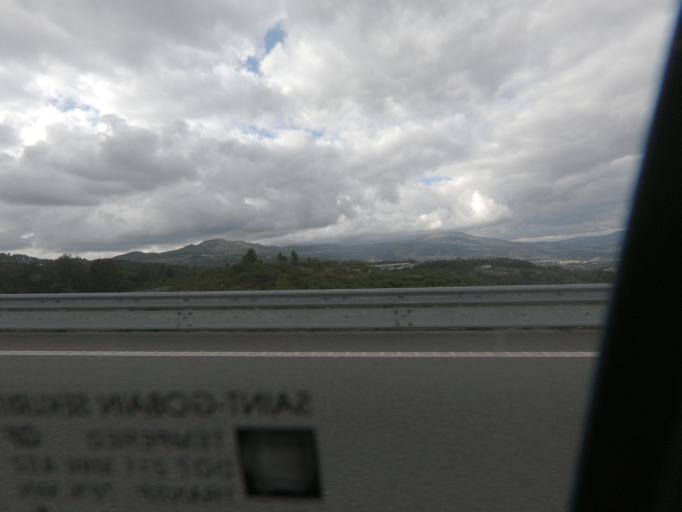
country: PT
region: Vila Real
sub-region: Santa Marta de Penaguiao
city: Santa Marta de Penaguiao
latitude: 41.2650
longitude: -7.8000
